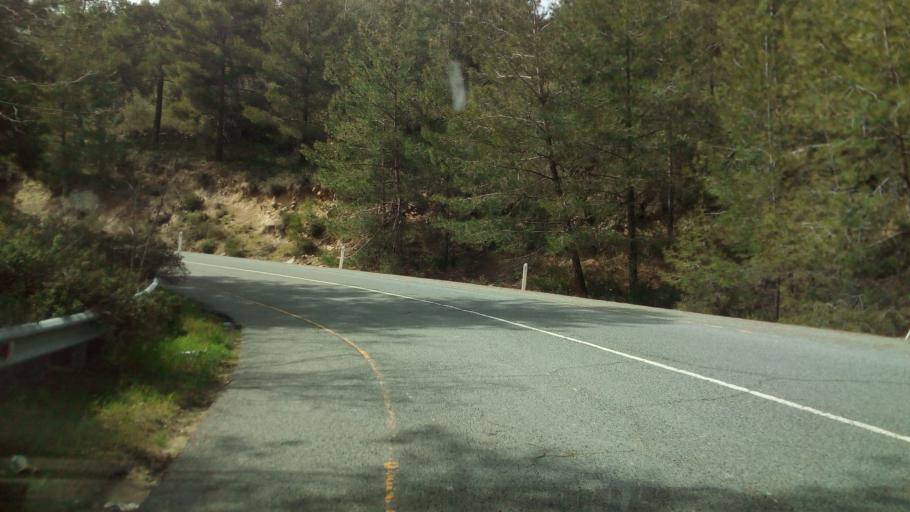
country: CY
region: Limassol
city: Pelendri
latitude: 34.8856
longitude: 32.9481
